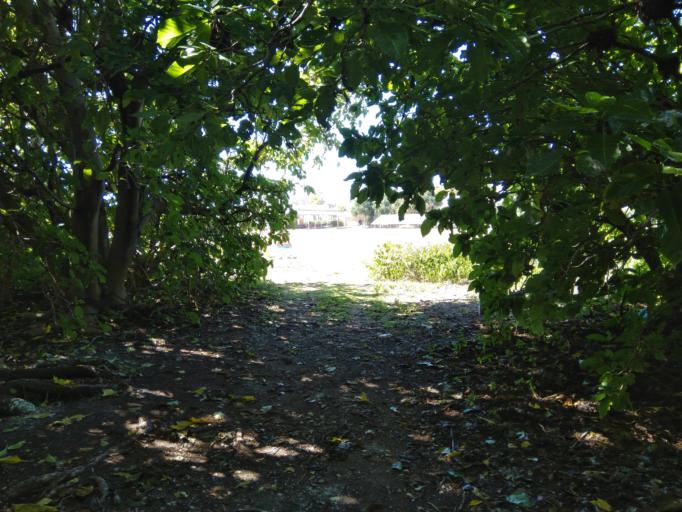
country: AU
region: Queensland
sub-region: Bundaberg
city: Bundaberg
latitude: -24.1139
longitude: 152.7149
